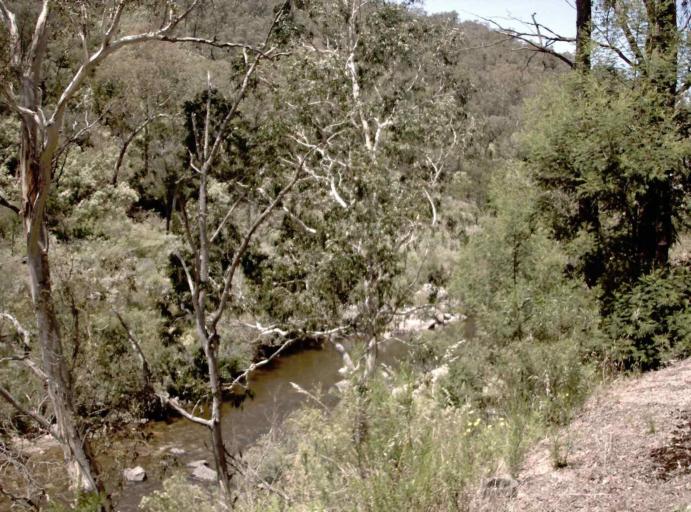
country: AU
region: Victoria
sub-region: East Gippsland
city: Bairnsdale
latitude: -37.4862
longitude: 147.8328
